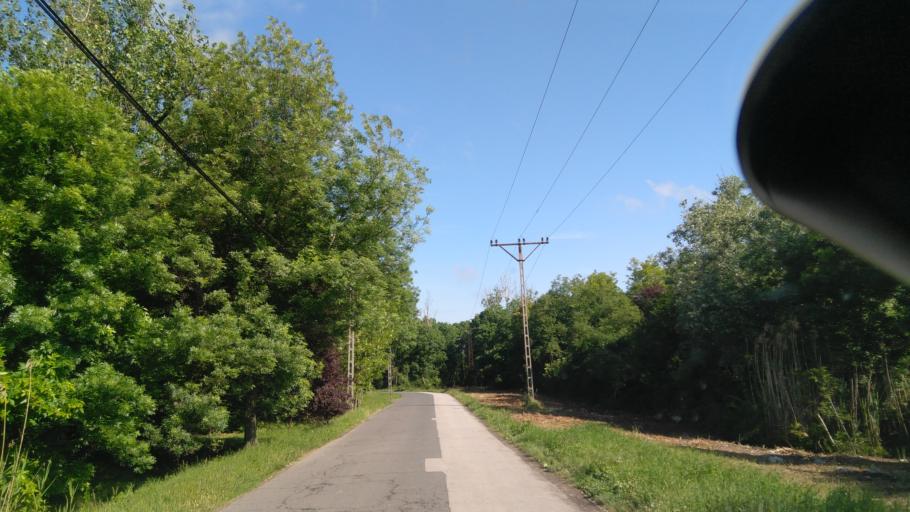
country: HU
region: Bekes
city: Bekes
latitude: 46.7810
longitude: 21.1348
